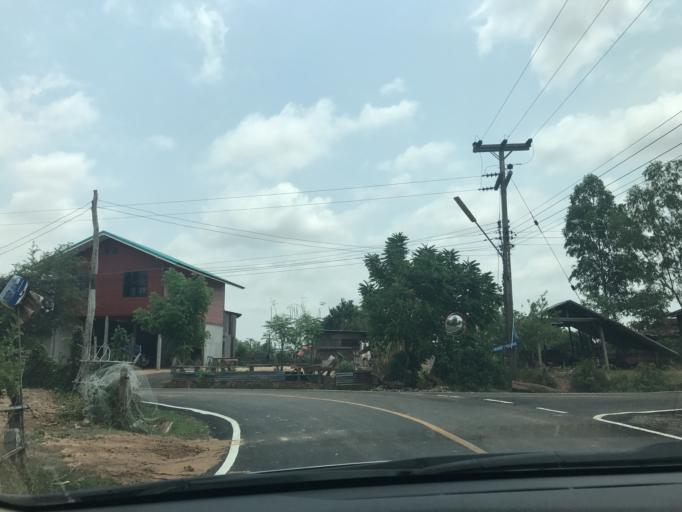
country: TH
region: Surin
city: Khwao Sinarin
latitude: 15.0402
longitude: 103.6509
